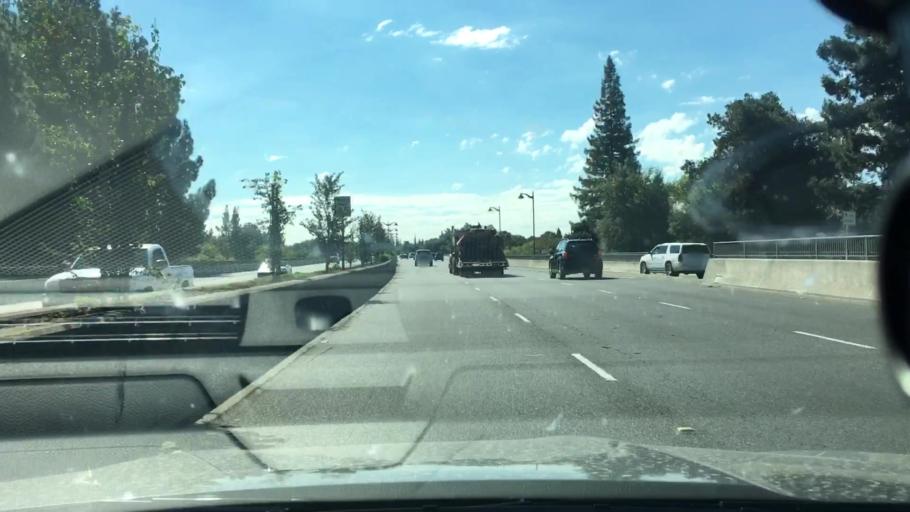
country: US
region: California
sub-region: Sacramento County
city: Rosemont
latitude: 38.5689
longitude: -121.3831
